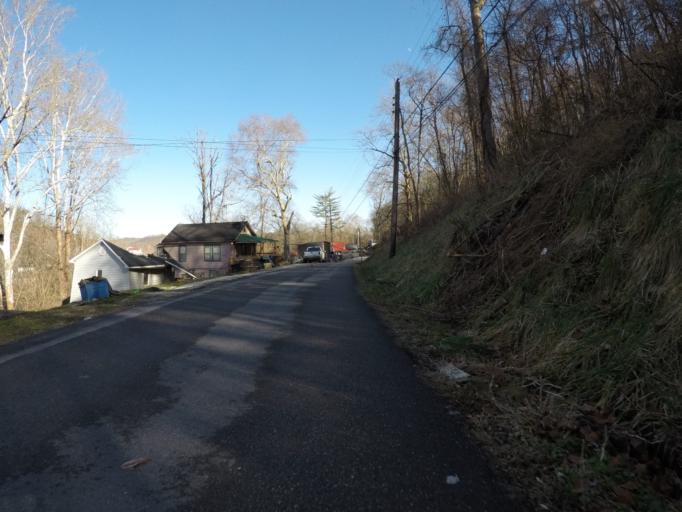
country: US
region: Kentucky
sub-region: Boyd County
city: Catlettsburg
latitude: 38.4191
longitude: -82.6056
